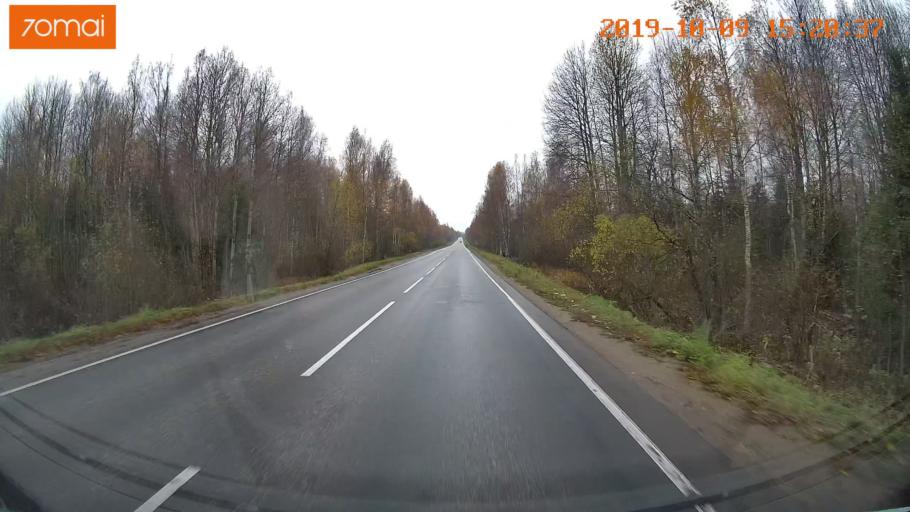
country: RU
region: Kostroma
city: Susanino
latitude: 58.0625
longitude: 41.5347
